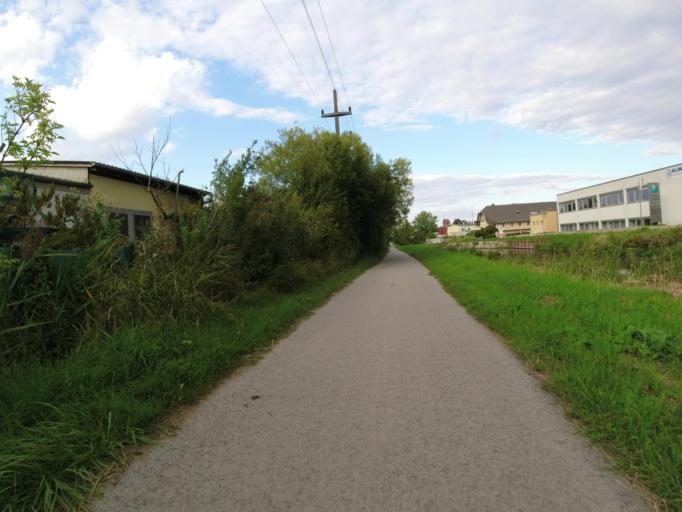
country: AT
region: Lower Austria
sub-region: Politischer Bezirk Modling
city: Guntramsdorf
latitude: 48.0411
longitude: 16.2965
